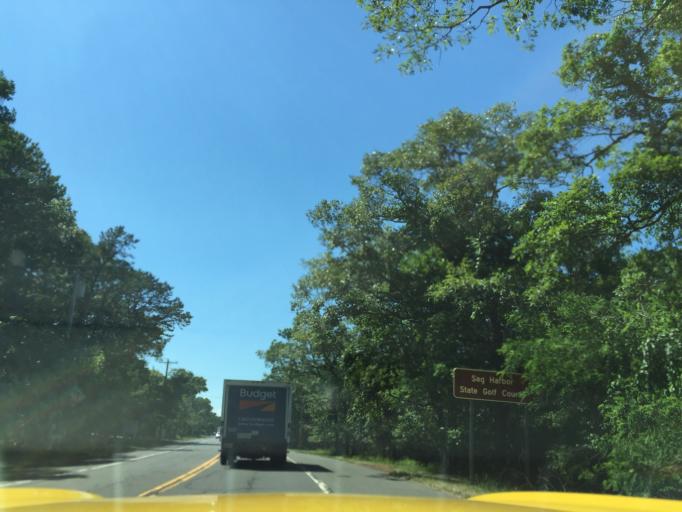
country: US
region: New York
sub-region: Suffolk County
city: Sag Harbor
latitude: 40.9916
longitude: -72.2673
